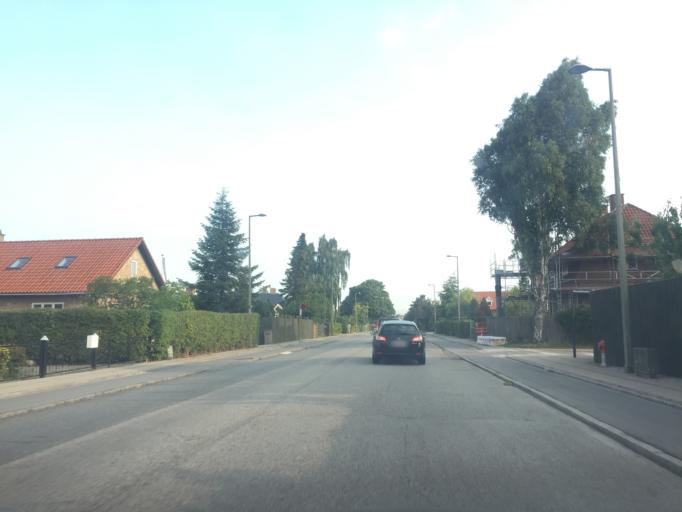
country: DK
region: Capital Region
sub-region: Kobenhavn
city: Vanlose
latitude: 55.7002
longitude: 12.4801
